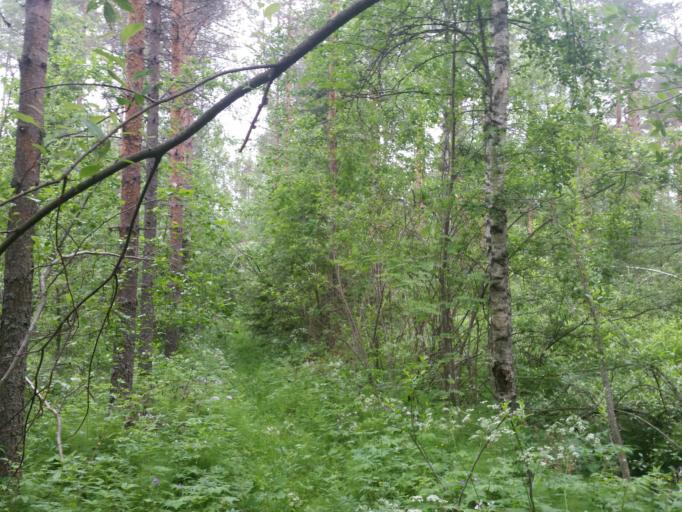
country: FI
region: Northern Savo
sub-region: Koillis-Savo
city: Kaavi
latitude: 62.9814
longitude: 28.7640
